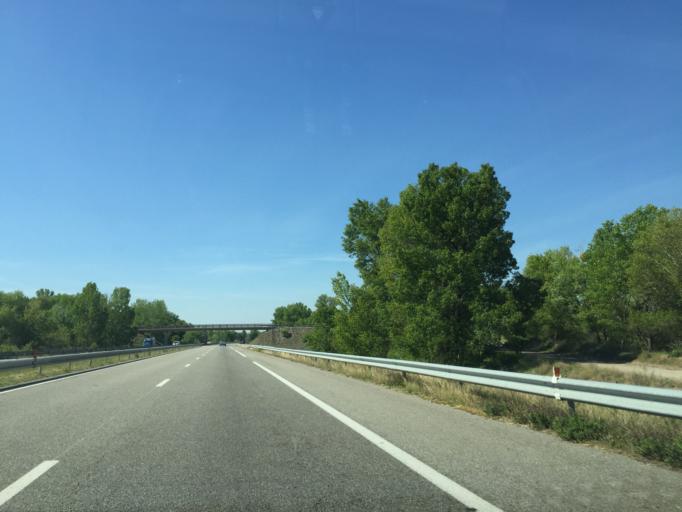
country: FR
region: Provence-Alpes-Cote d'Azur
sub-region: Departement des Alpes-de-Haute-Provence
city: Villeneuve
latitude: 43.8730
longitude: 5.8733
